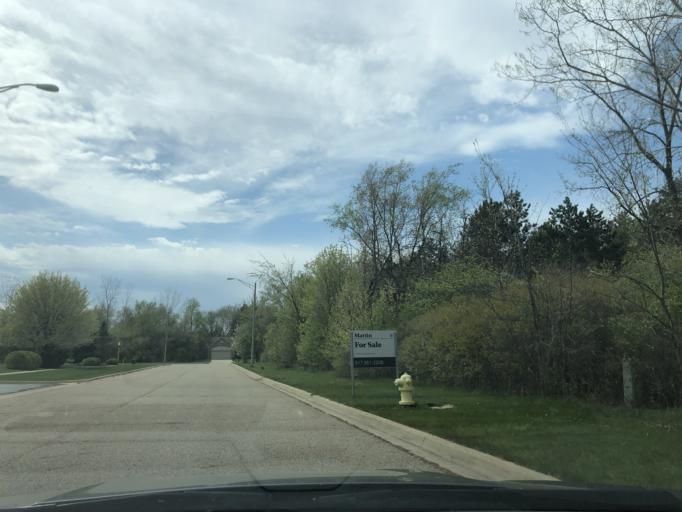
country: US
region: Michigan
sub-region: Eaton County
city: Waverly
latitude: 42.7244
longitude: -84.6491
